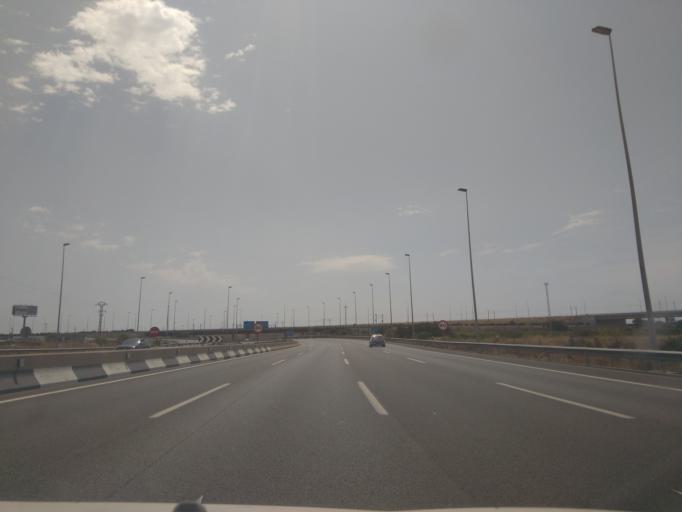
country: ES
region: Valencia
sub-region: Provincia de Valencia
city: Silla
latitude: 39.3518
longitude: -0.4272
